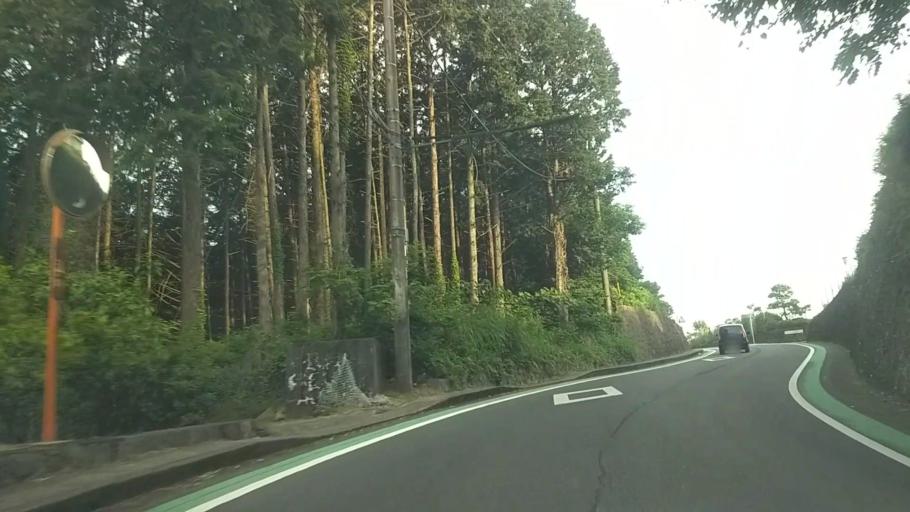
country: JP
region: Kanagawa
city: Odawara
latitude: 35.3256
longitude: 139.1078
